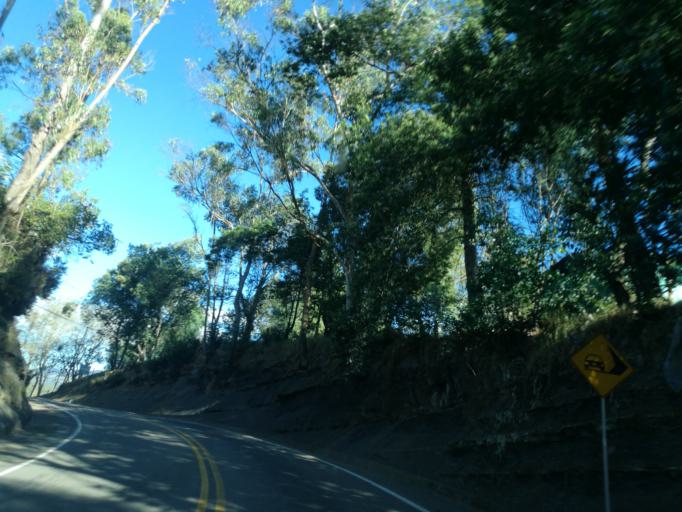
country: CO
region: Boyaca
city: Chiquinquira
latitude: 5.6211
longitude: -73.7790
